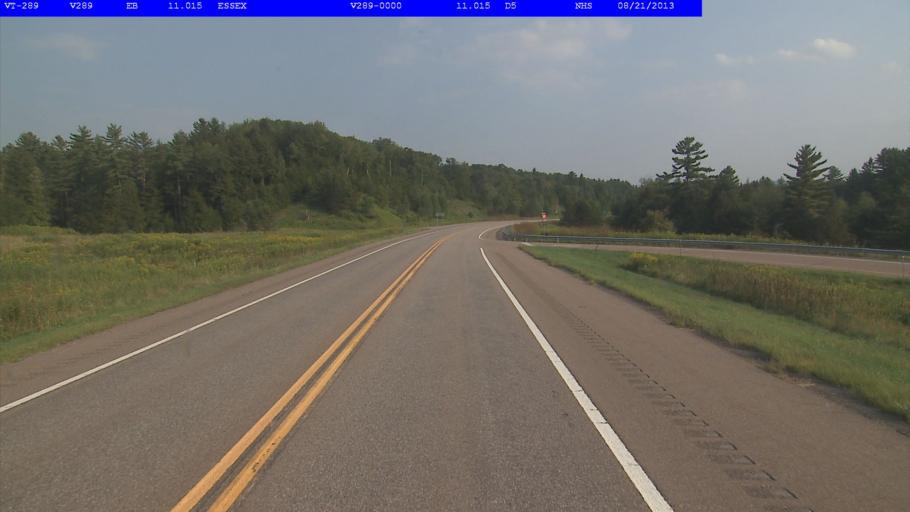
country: US
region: Vermont
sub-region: Chittenden County
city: Essex Junction
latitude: 44.4933
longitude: -73.0658
